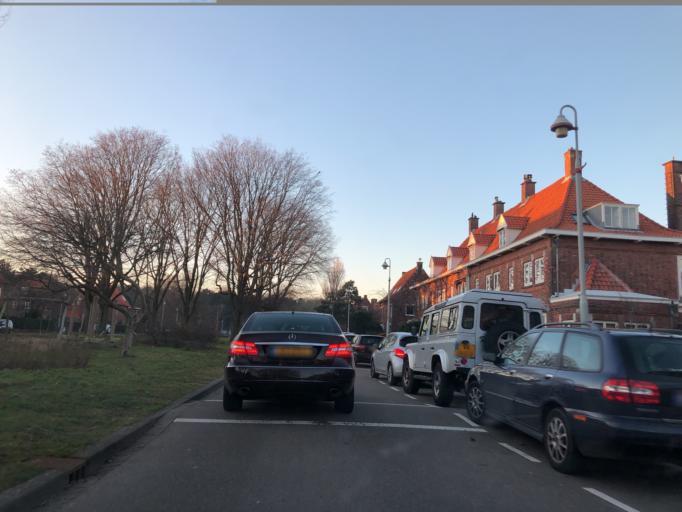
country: NL
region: South Holland
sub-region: Gemeente Den Haag
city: Scheveningen
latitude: 52.0796
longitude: 4.2527
